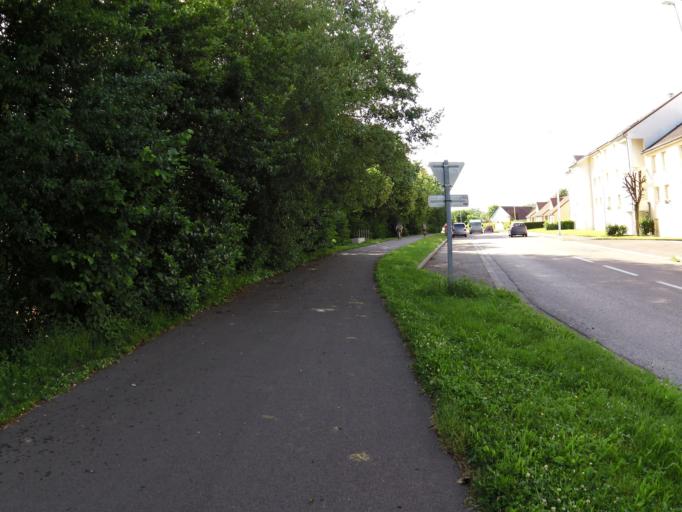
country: FR
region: Champagne-Ardenne
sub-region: Departement de l'Aube
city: Saint-Julien-les-Villas
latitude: 48.2827
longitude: 4.0926
